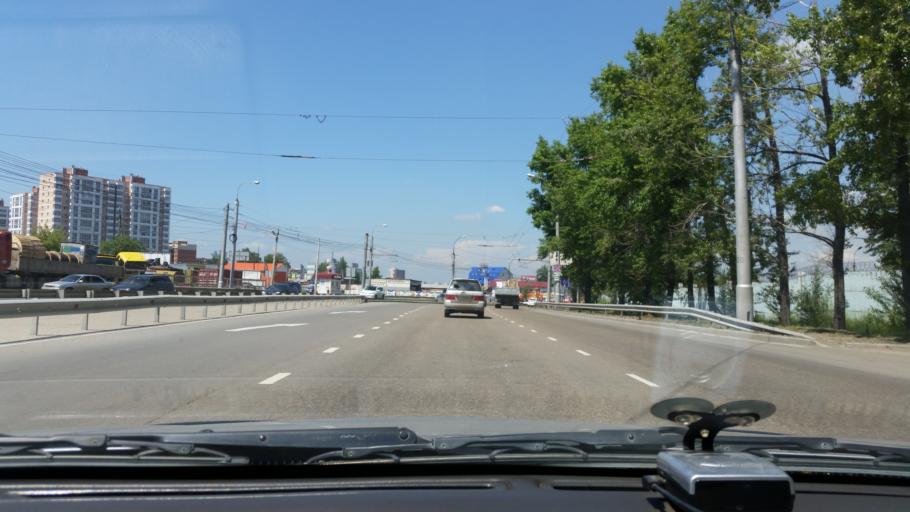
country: RU
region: Irkutsk
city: Dzerzhinsk
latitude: 52.2650
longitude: 104.3483
